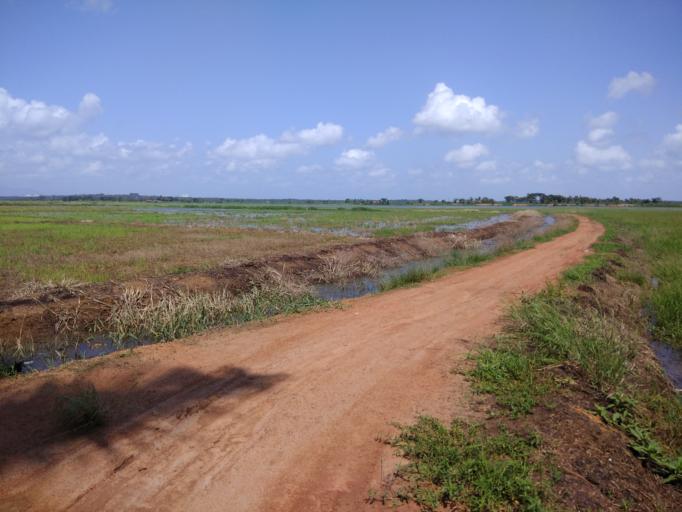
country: IN
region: Kerala
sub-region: Thrissur District
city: Trichur
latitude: 10.5356
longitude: 76.1446
